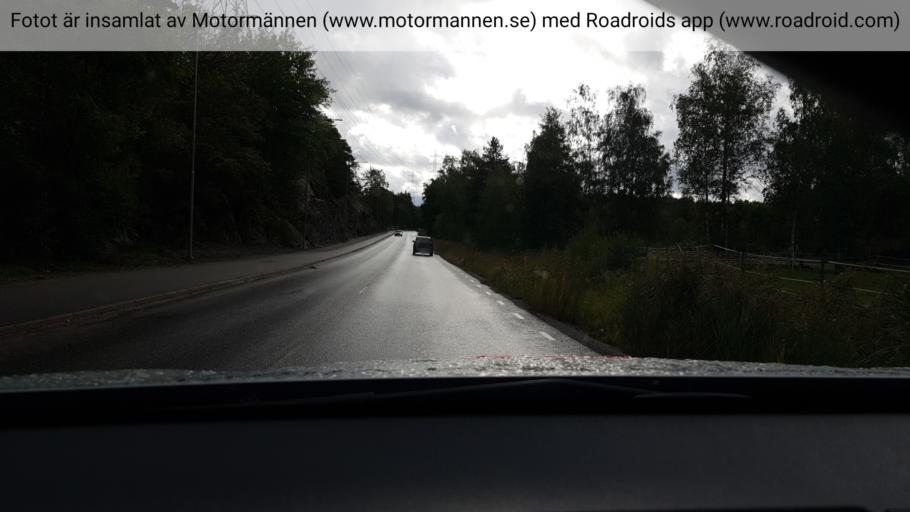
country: SE
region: Stockholm
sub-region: Huddinge Kommun
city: Huddinge
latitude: 59.2393
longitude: 18.0289
